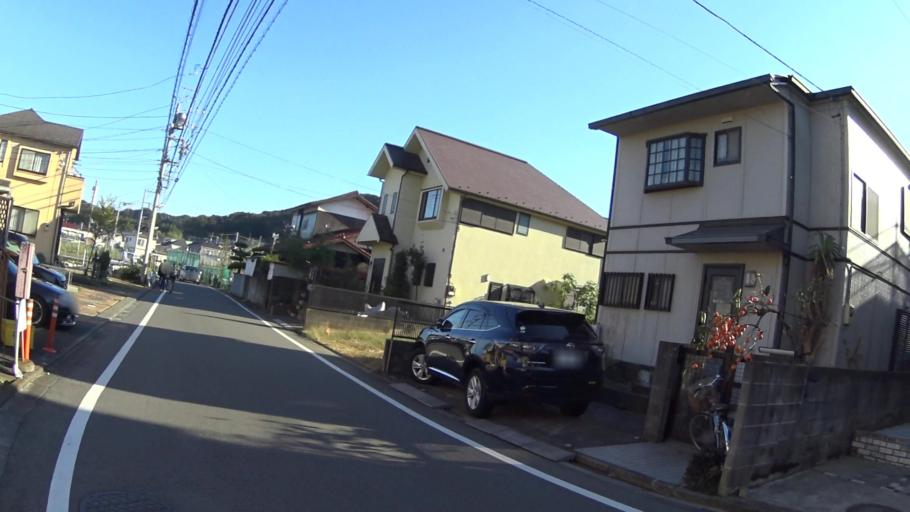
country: JP
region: Tokyo
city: Chofugaoka
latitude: 35.6350
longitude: 139.5074
